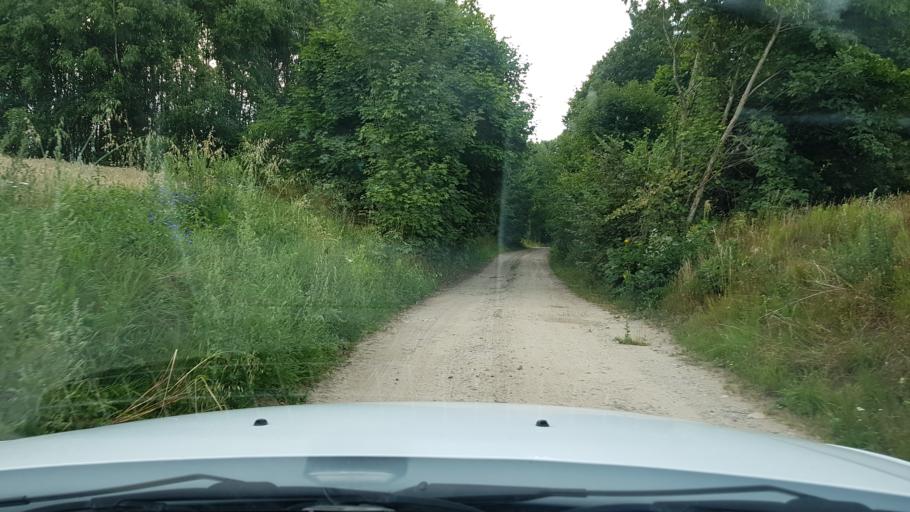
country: PL
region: West Pomeranian Voivodeship
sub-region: Powiat swidwinski
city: Polczyn-Zdroj
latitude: 53.8005
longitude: 16.0765
